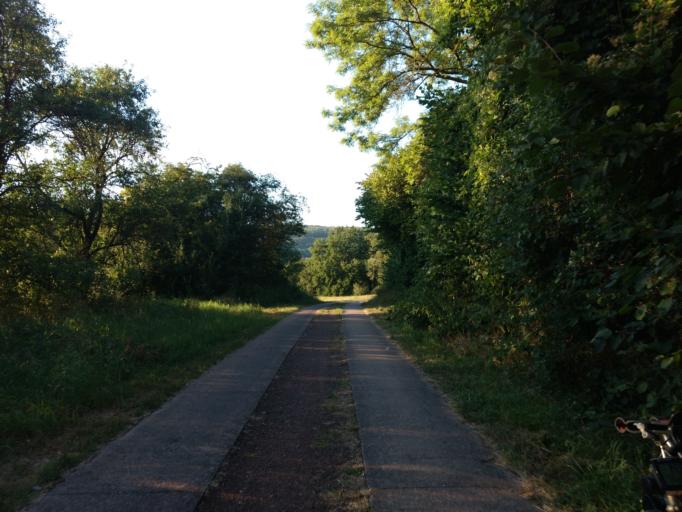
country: DE
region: Saarland
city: Rehlingen-Siersburg
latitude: 49.3575
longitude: 6.6292
